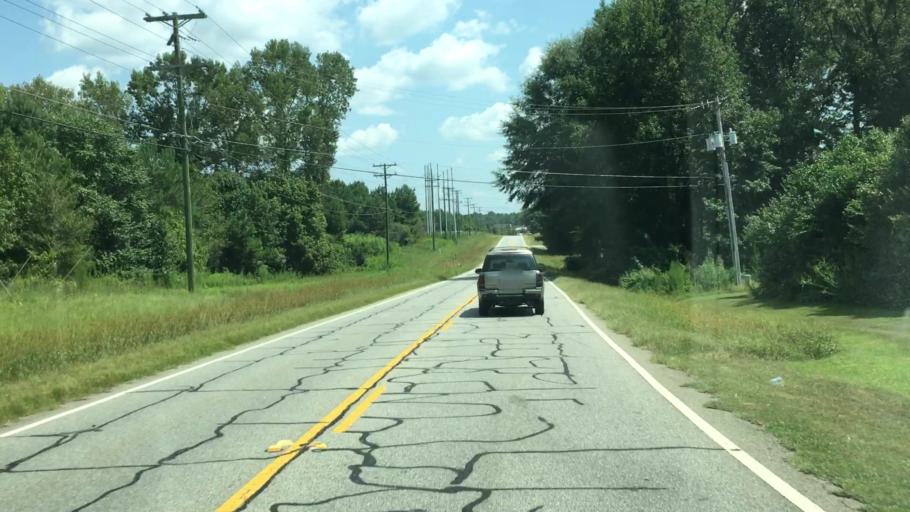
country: US
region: Georgia
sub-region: Barrow County
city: Statham
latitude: 33.9042
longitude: -83.5798
